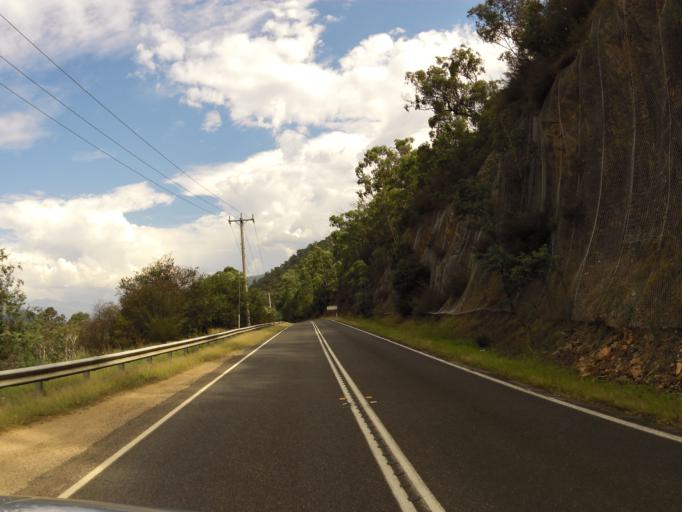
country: AU
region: Victoria
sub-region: Alpine
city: Mount Beauty
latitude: -36.7466
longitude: 147.0163
